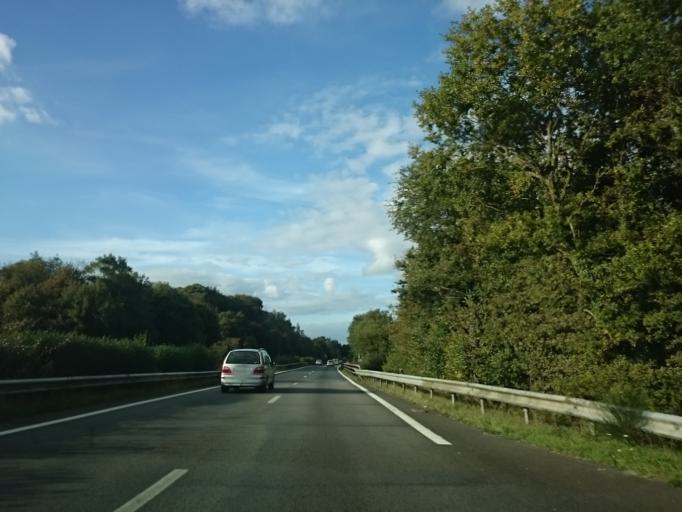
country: FR
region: Pays de la Loire
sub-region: Departement de la Loire-Atlantique
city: Nozay
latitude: 47.5578
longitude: -1.6337
